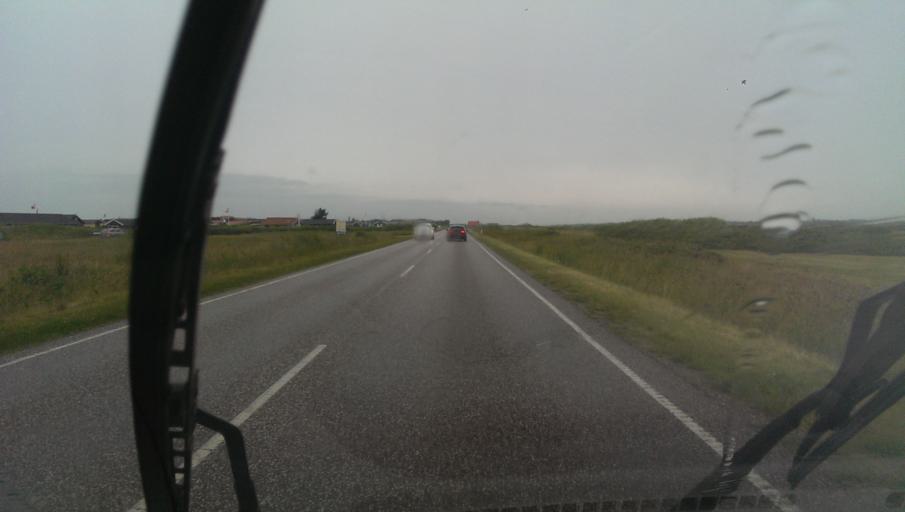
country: DK
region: Central Jutland
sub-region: Ringkobing-Skjern Kommune
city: Hvide Sande
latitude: 56.1278
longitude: 8.1184
